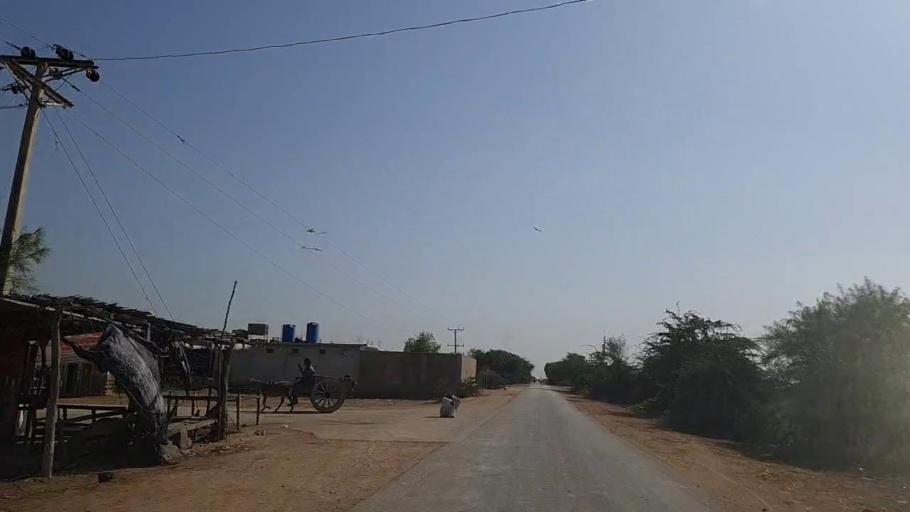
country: PK
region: Sindh
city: Mirpur Batoro
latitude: 24.6402
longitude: 68.2909
